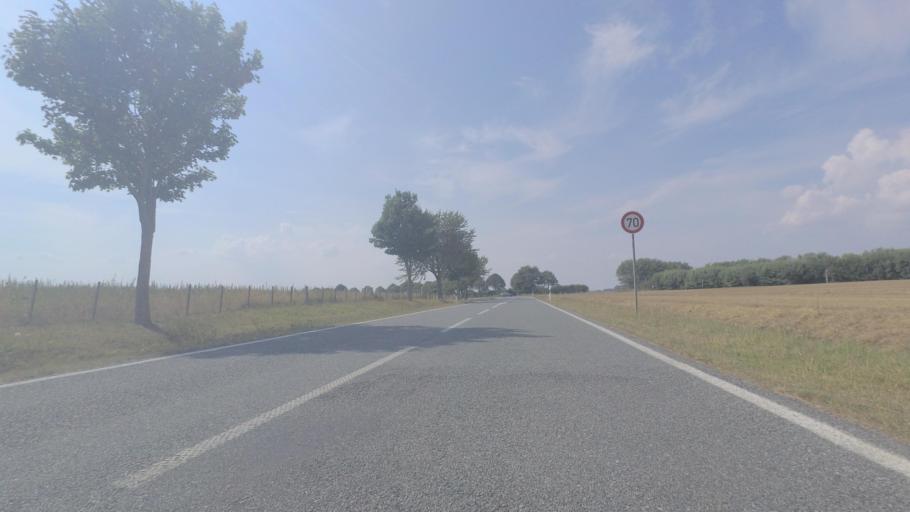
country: DE
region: Mecklenburg-Vorpommern
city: Poseritz
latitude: 54.2309
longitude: 13.2804
